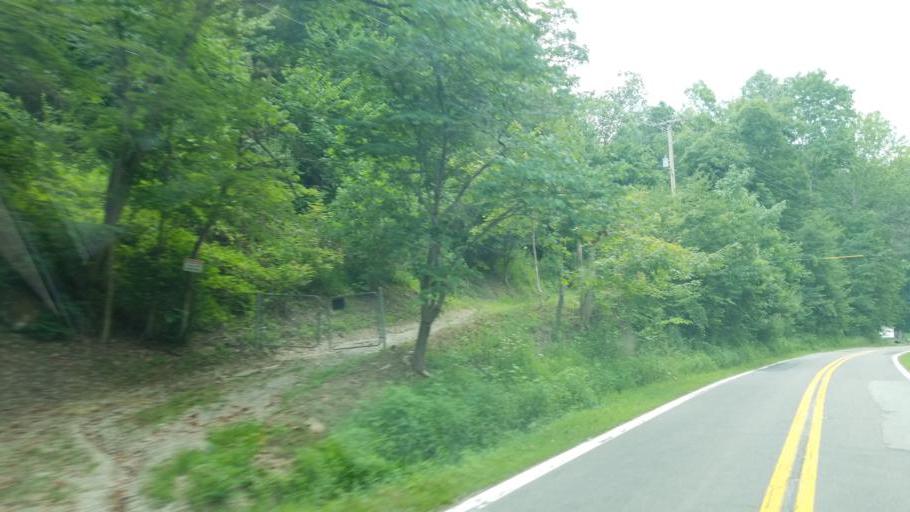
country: US
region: West Virginia
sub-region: Kanawha County
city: Alum Creek
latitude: 38.2836
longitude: -81.7765
